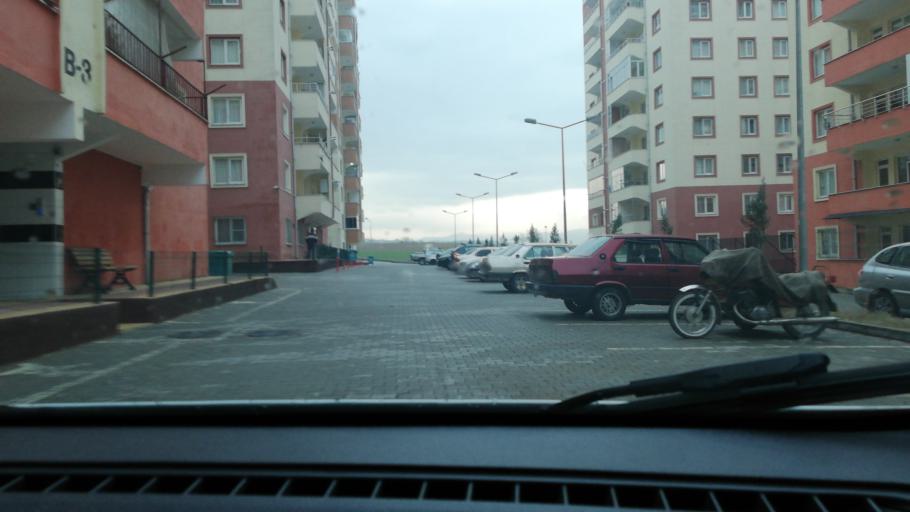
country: TR
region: Kahramanmaras
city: Kahramanmaras
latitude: 37.5801
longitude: 36.9992
